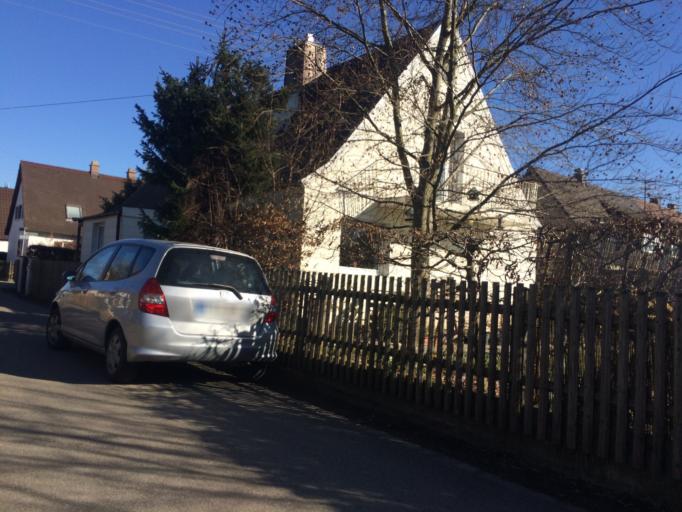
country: DE
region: Bavaria
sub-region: Swabia
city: Augsburg
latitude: 48.4005
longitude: 10.9144
